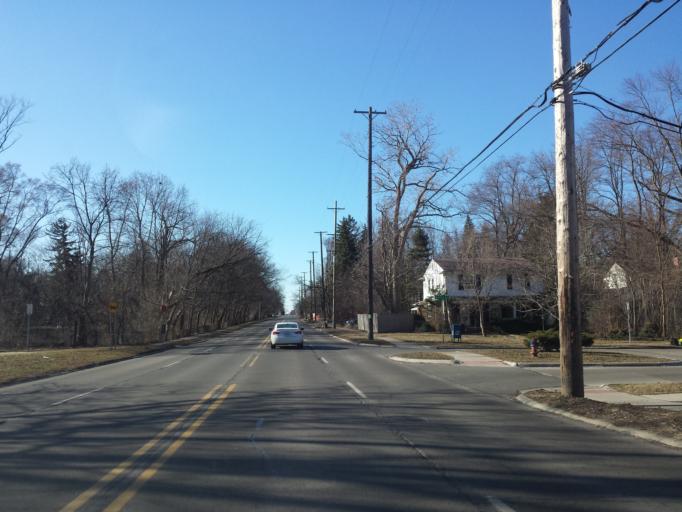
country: US
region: Michigan
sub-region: Oakland County
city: Clawson
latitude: 42.5116
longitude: -83.1452
